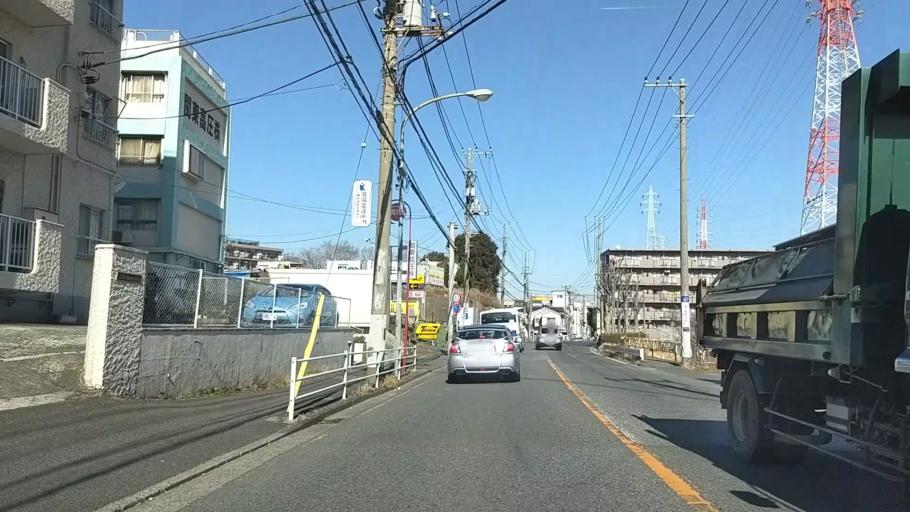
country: JP
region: Kanagawa
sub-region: Kawasaki-shi
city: Kawasaki
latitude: 35.5203
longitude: 139.6495
